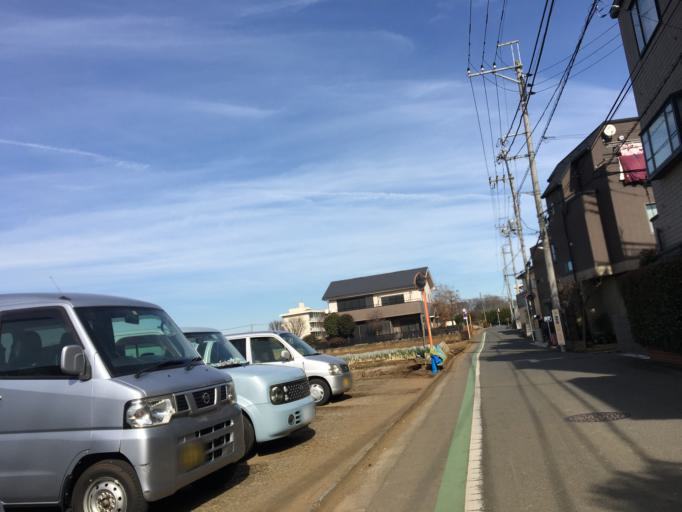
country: JP
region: Saitama
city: Oi
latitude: 35.8314
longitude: 139.5365
